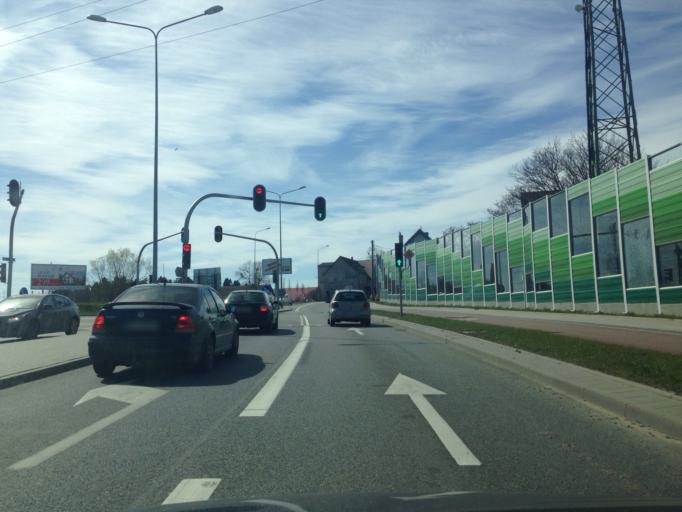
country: PL
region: Pomeranian Voivodeship
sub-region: Gdynia
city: Wielki Kack
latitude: 54.5005
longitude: 18.4615
